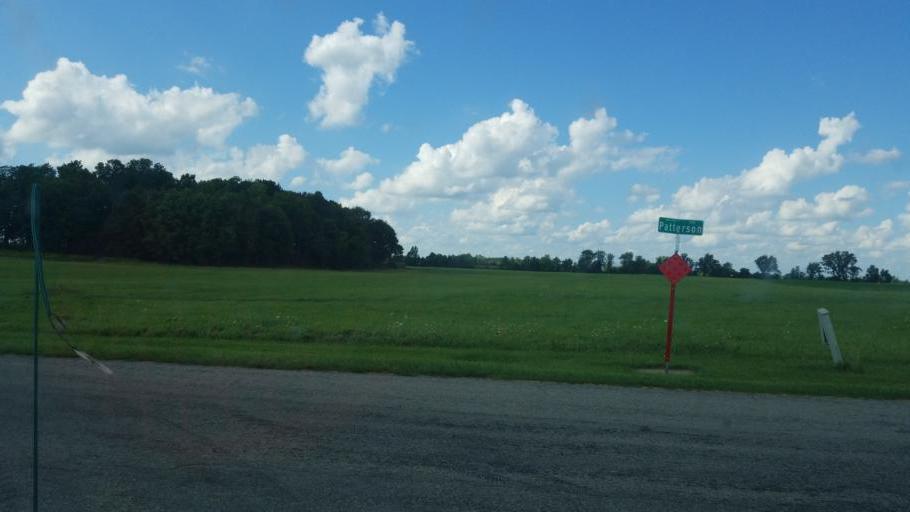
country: US
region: Ohio
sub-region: Union County
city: Richwood
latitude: 40.5010
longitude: -83.3470
